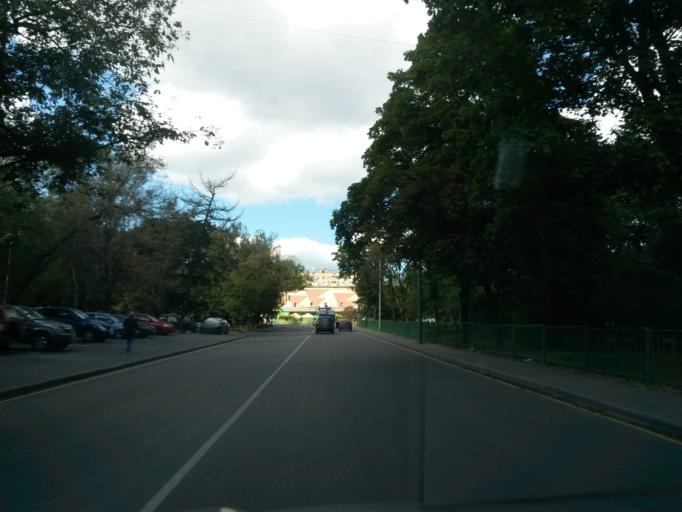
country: RU
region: Moskovskaya
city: Kozhukhovo
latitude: 55.7018
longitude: 37.6743
